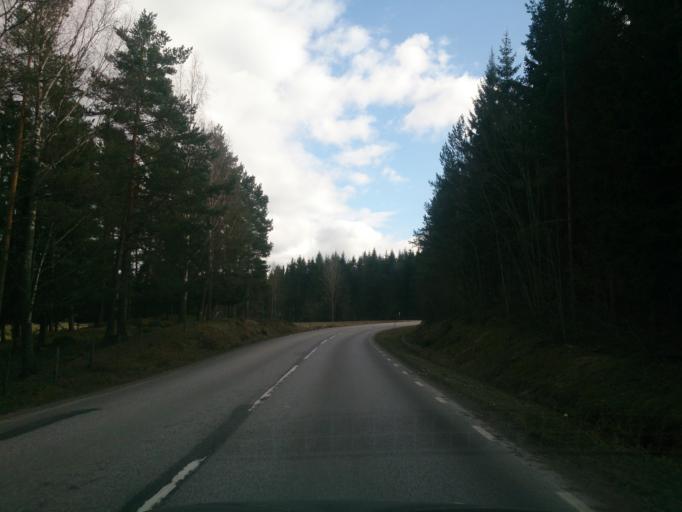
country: SE
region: OEstergoetland
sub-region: Atvidabergs Kommun
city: Atvidaberg
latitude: 58.3557
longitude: 16.0336
